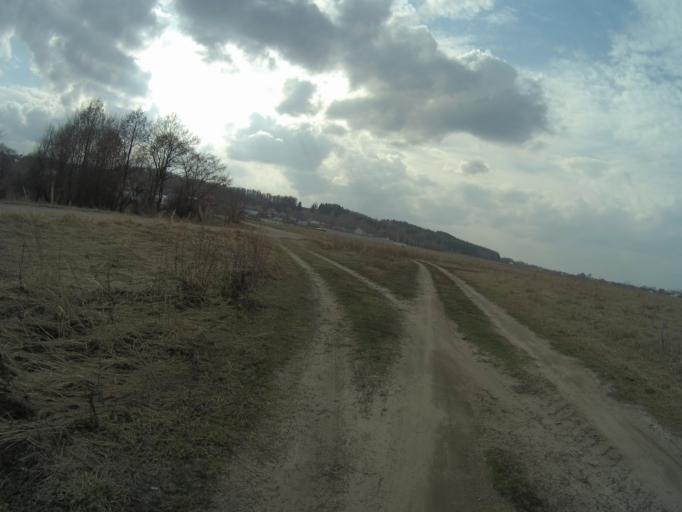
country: RU
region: Vladimir
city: Raduzhnyy
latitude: 56.0183
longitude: 40.3492
